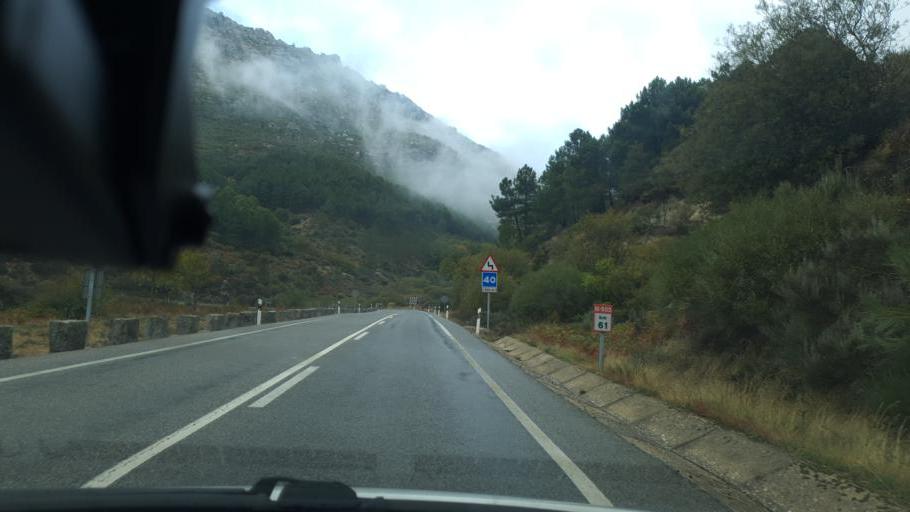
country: ES
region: Castille and Leon
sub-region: Provincia de Avila
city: Cuevas del Valle
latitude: 40.3074
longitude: -5.0123
